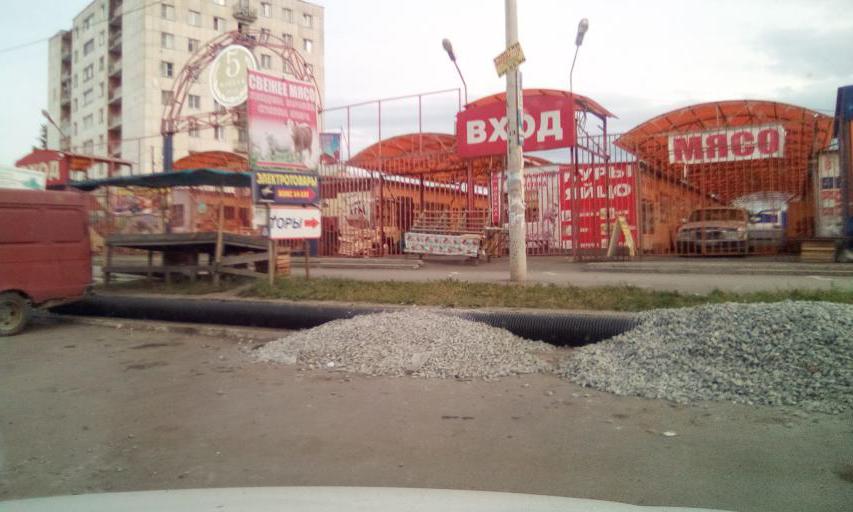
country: RU
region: Chelyabinsk
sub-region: Gorod Chelyabinsk
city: Chelyabinsk
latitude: 55.1667
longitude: 61.4547
